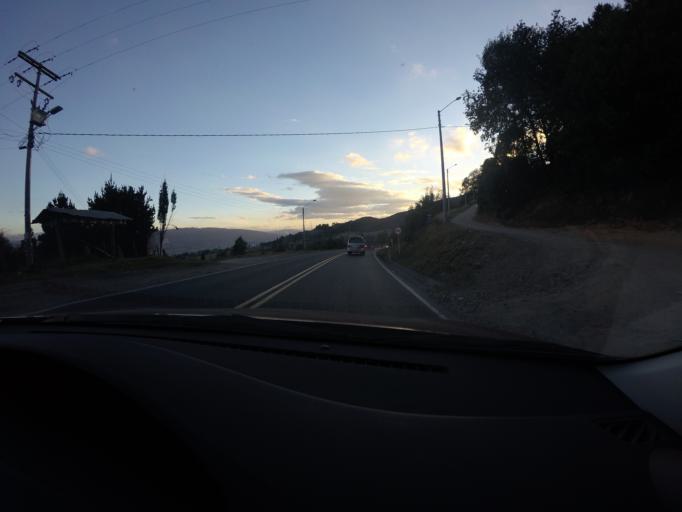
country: CO
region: Cundinamarca
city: Nemocon
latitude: 5.1523
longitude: -73.9011
